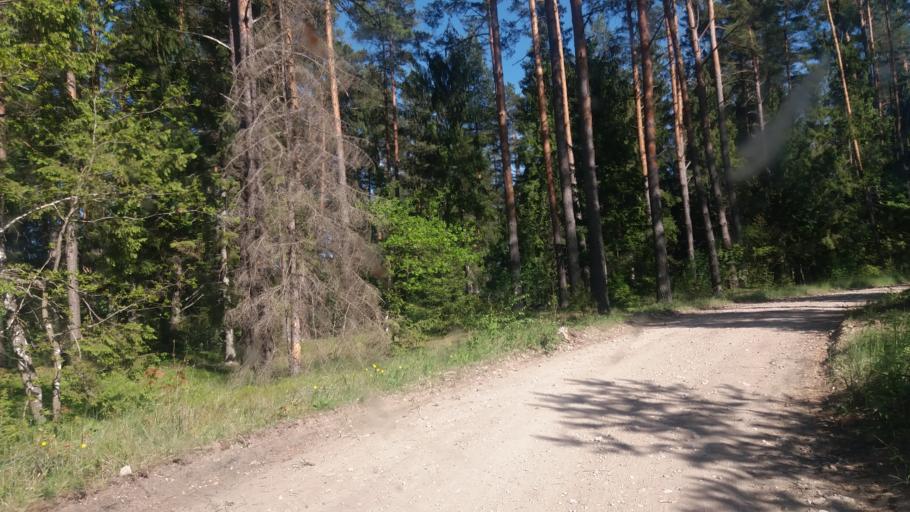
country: LV
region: Kuldigas Rajons
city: Kuldiga
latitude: 57.0793
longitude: 21.8078
